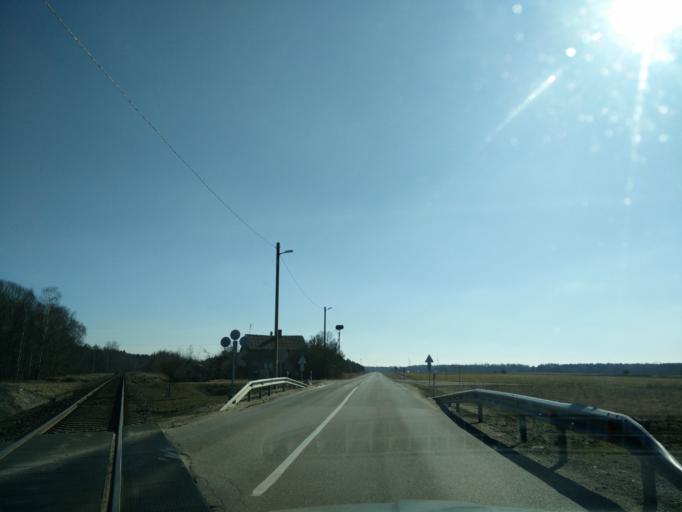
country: LT
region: Klaipedos apskritis
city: Silute
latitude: 55.3265
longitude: 21.5240
